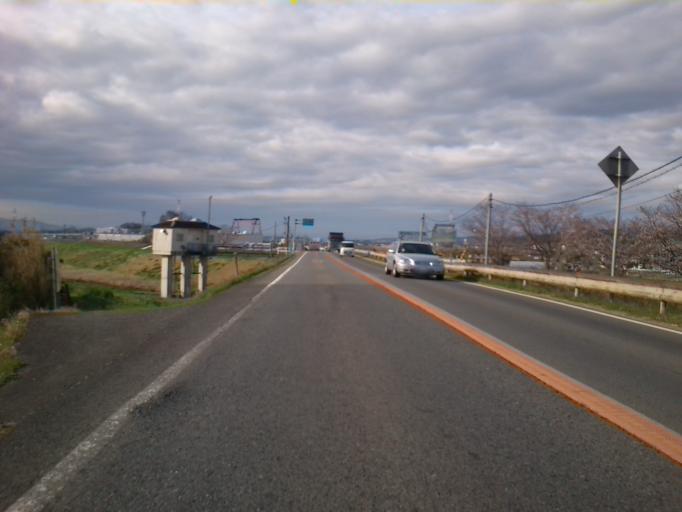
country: JP
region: Kyoto
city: Tanabe
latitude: 34.7877
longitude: 135.8059
